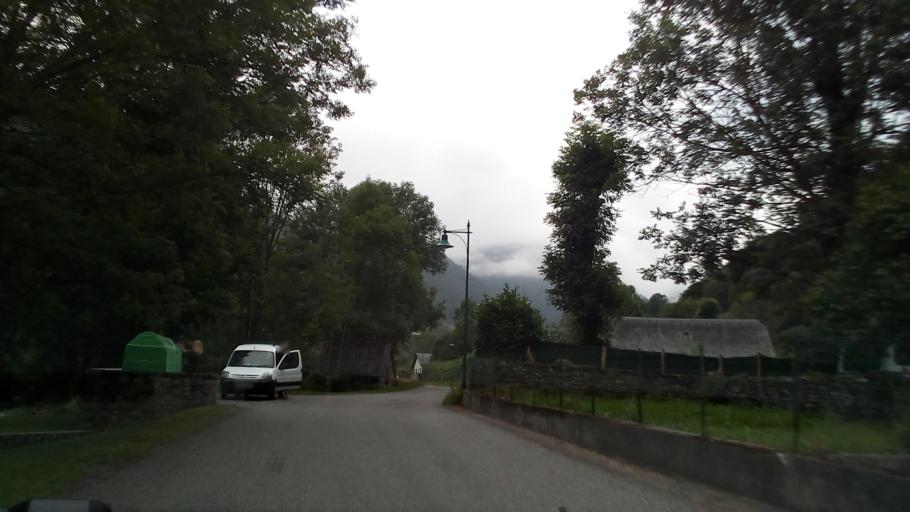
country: FR
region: Midi-Pyrenees
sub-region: Departement des Hautes-Pyrenees
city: Cauterets
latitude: 42.9391
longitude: -0.1784
